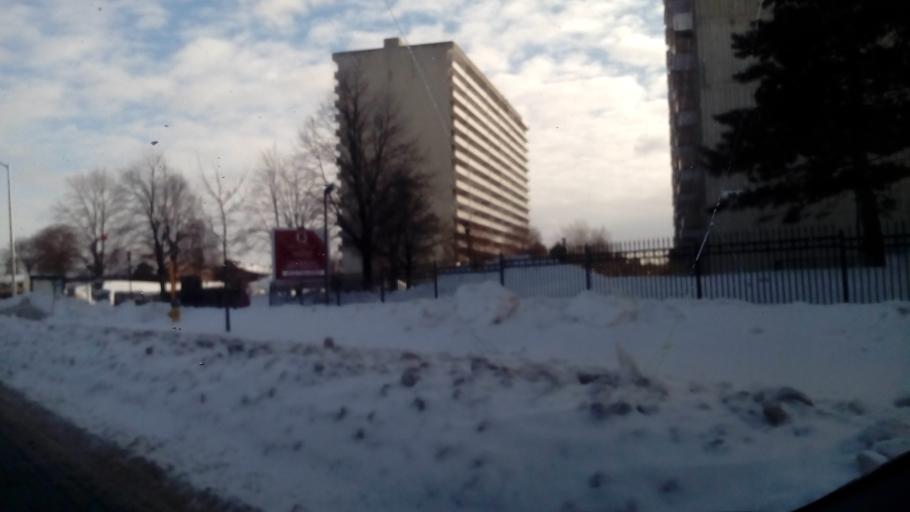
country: CA
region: Ontario
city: Ottawa
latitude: 45.4289
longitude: -75.6367
